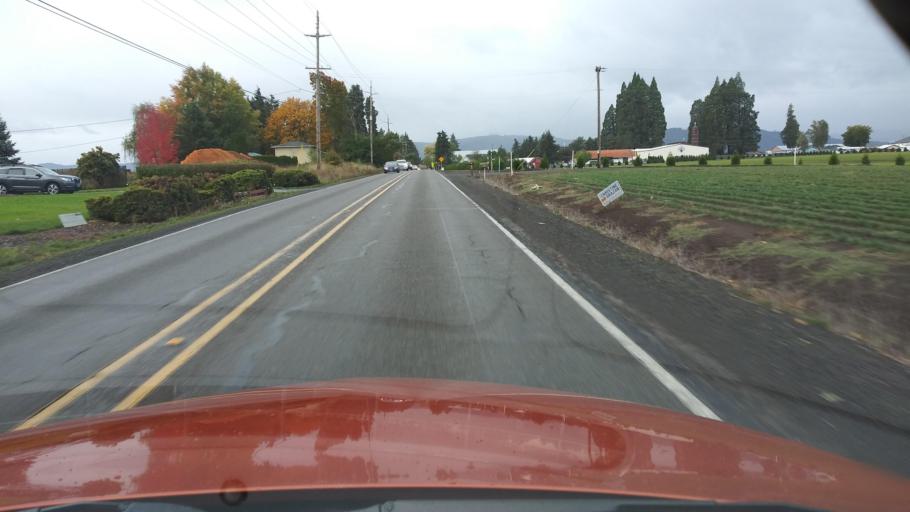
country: US
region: Oregon
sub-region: Washington County
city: Cornelius
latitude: 45.5509
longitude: -123.0790
